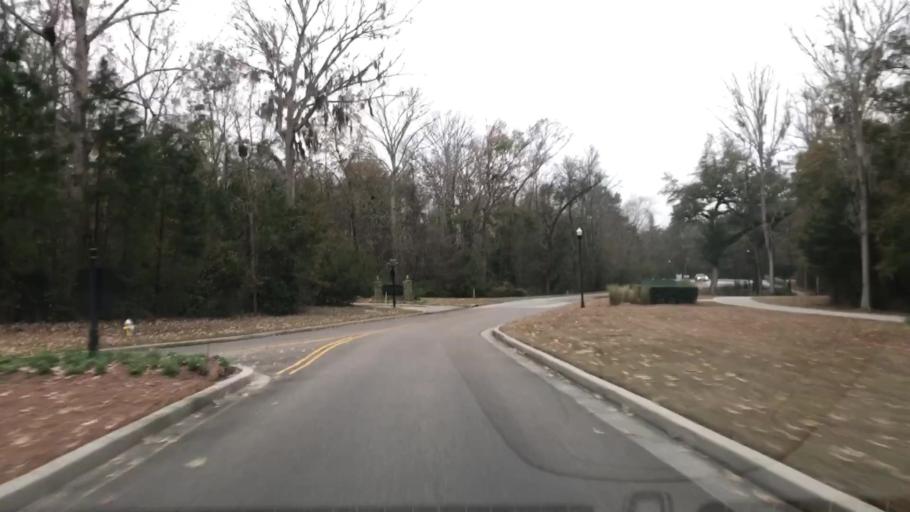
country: US
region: South Carolina
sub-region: Charleston County
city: Shell Point
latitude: 32.8064
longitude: -80.0787
